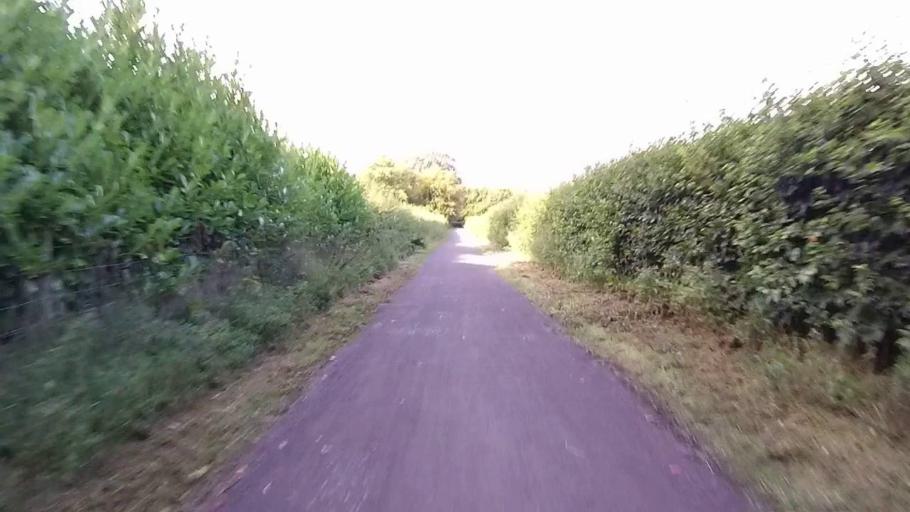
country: GB
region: Scotland
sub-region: Perth and Kinross
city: Kinross
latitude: 56.2021
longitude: -3.4069
